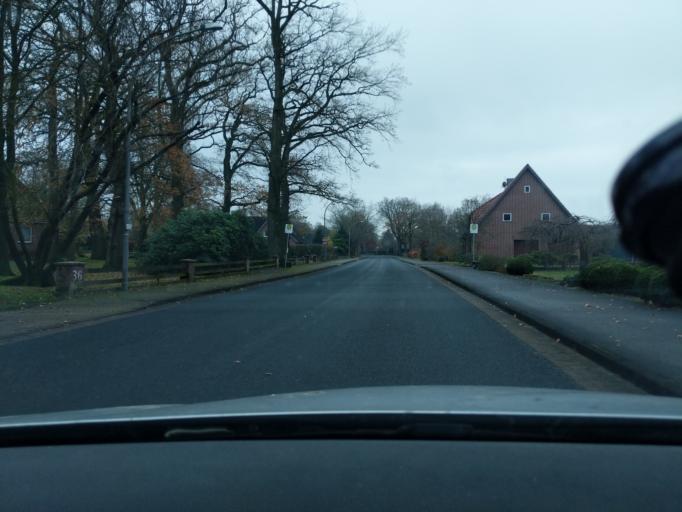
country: DE
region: Lower Saxony
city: Ahlerstedt
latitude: 53.3501
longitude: 9.4009
